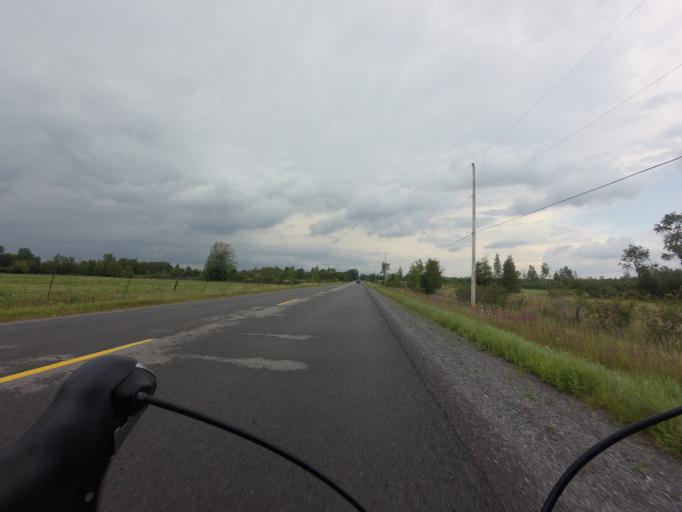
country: CA
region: Ontario
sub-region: Lanark County
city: Smiths Falls
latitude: 44.8489
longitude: -75.8141
